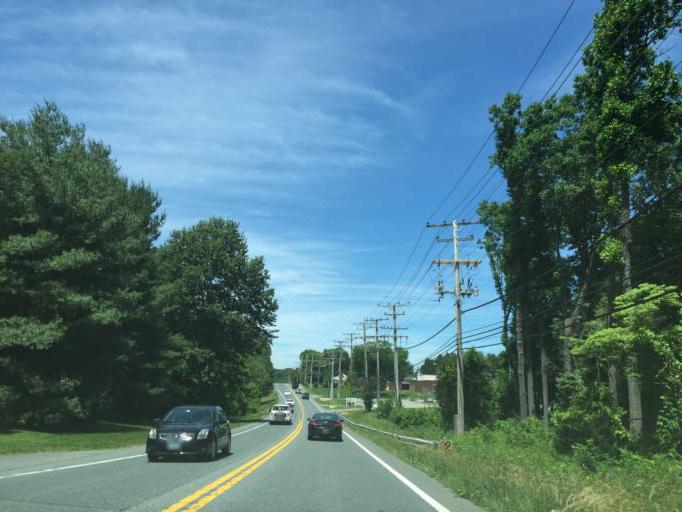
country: US
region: Maryland
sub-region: Harford County
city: South Bel Air
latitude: 39.5524
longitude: -76.3207
